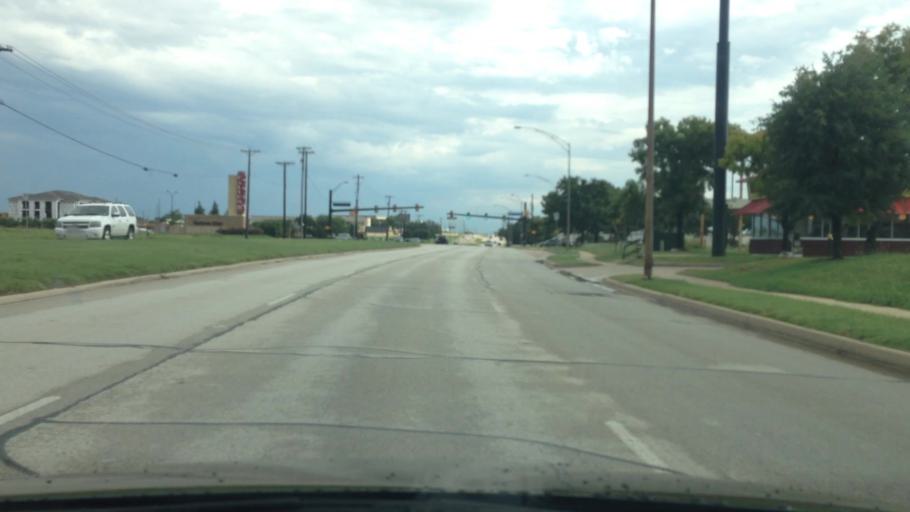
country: US
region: Texas
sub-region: Tarrant County
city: Watauga
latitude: 32.8365
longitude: -97.2906
